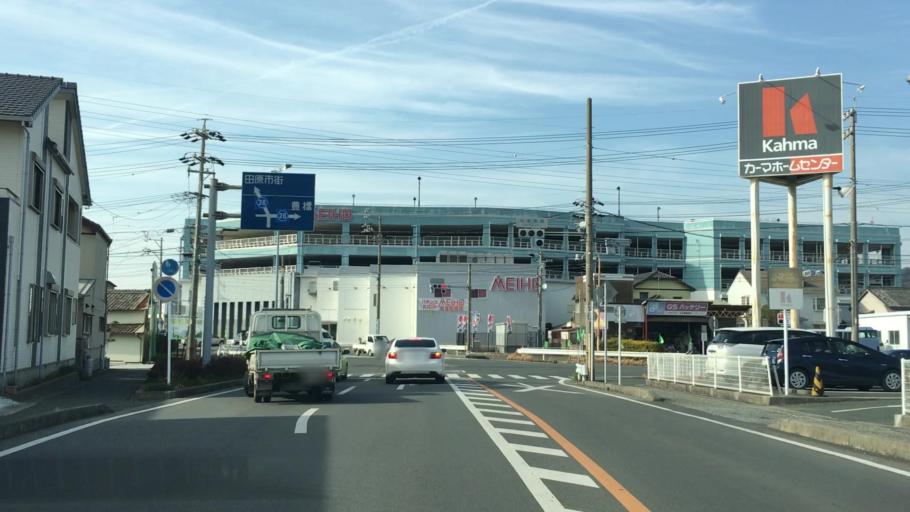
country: JP
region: Aichi
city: Tahara
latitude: 34.6672
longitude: 137.2745
